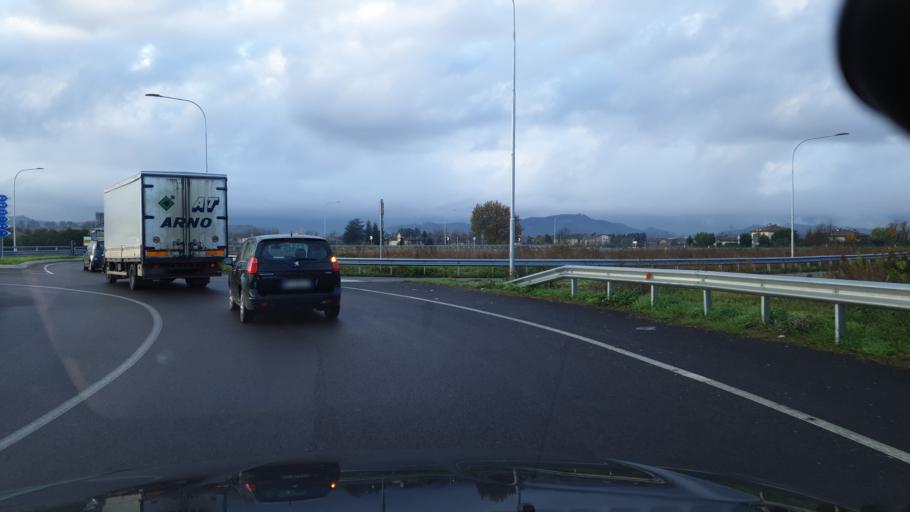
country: IT
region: Emilia-Romagna
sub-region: Provincia di Bologna
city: Crespellano
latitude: 44.5161
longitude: 11.1134
